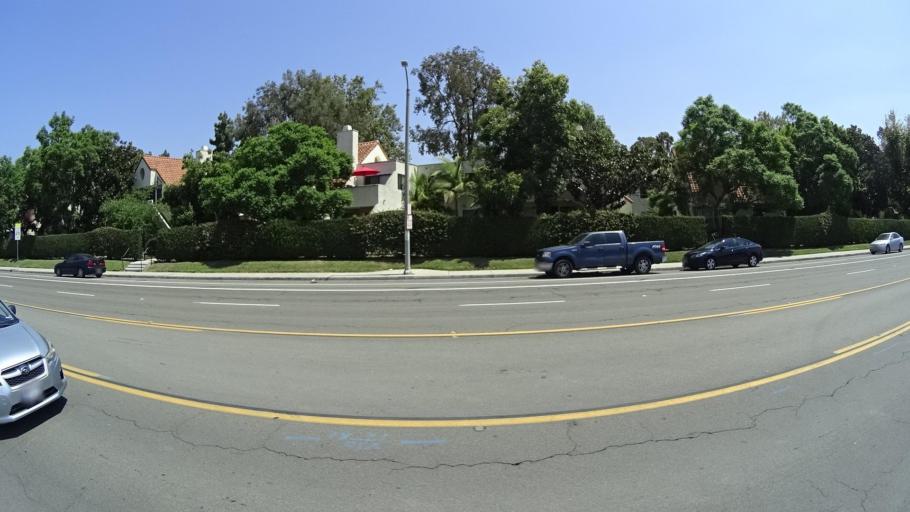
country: US
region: California
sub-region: San Diego County
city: Vista
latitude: 33.2022
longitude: -117.2554
